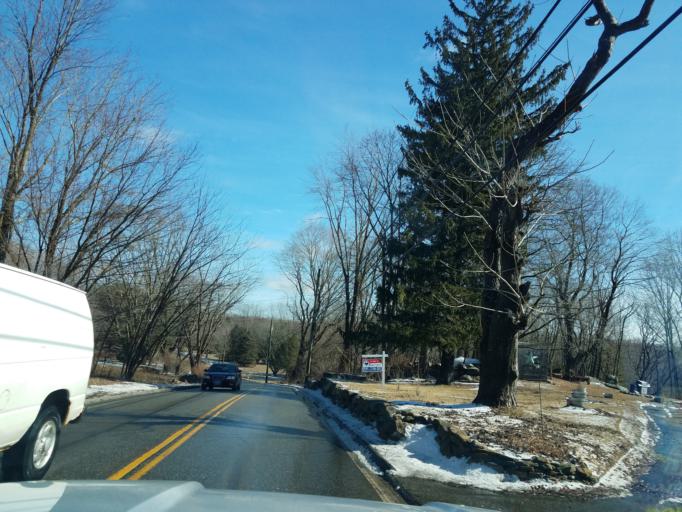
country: US
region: Connecticut
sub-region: New London County
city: Ledyard Center
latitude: 41.4459
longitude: -72.0046
